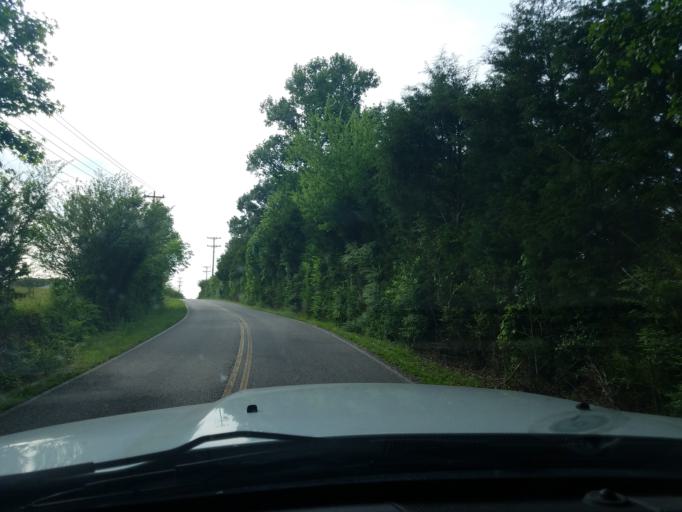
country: US
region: Tennessee
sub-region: Putnam County
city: Baxter
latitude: 36.1307
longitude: -85.5727
